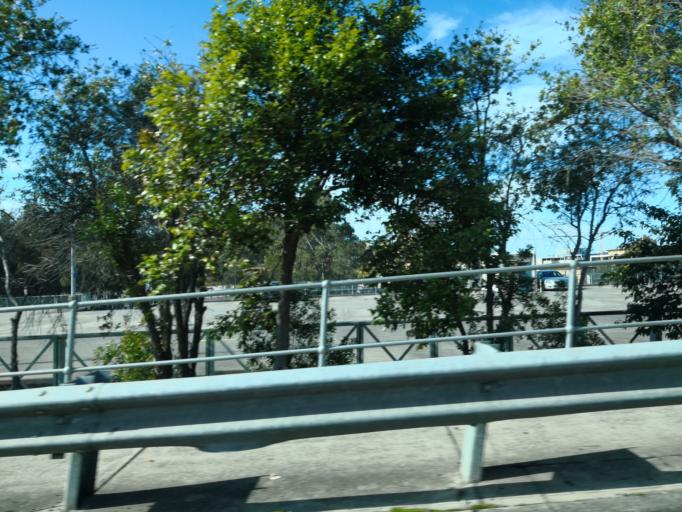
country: AU
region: New South Wales
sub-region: Gosford Shire
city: Gosford
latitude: -33.4248
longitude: 151.3404
